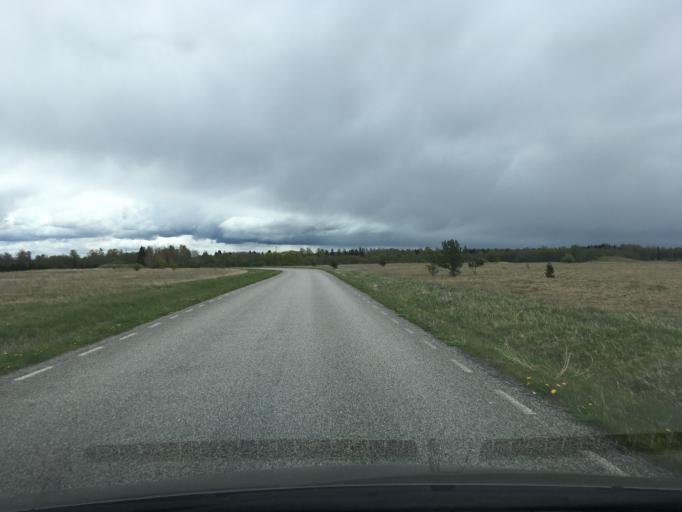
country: EE
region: Harju
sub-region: Rae vald
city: Vaida
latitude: 59.3542
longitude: 24.9856
